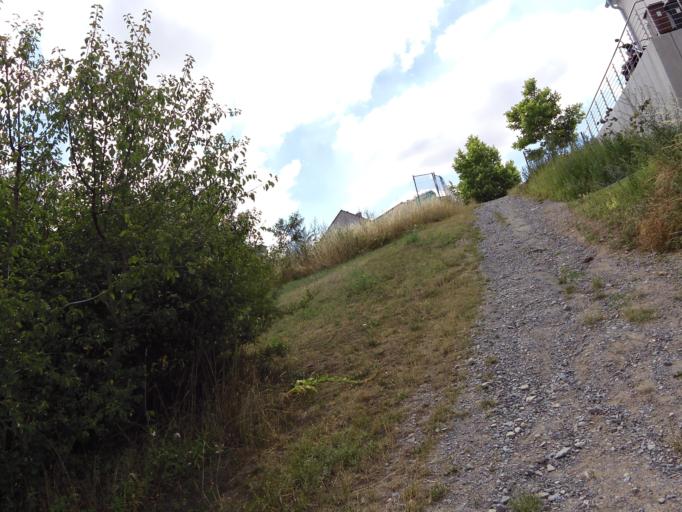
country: DE
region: Bavaria
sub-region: Regierungsbezirk Unterfranken
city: Gerbrunn
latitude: 49.7851
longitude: 9.9903
